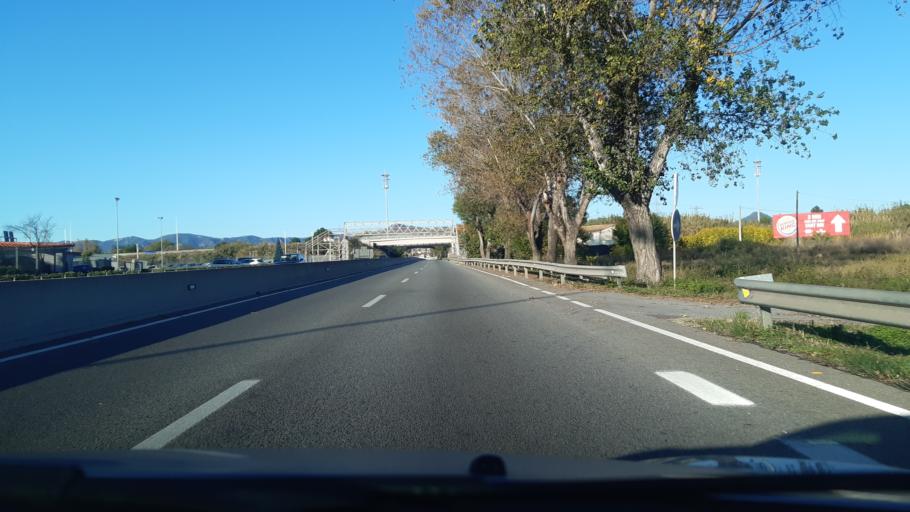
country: ES
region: Catalonia
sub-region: Provincia de Barcelona
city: Cornella de Llobregat
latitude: 41.3316
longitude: 2.0743
